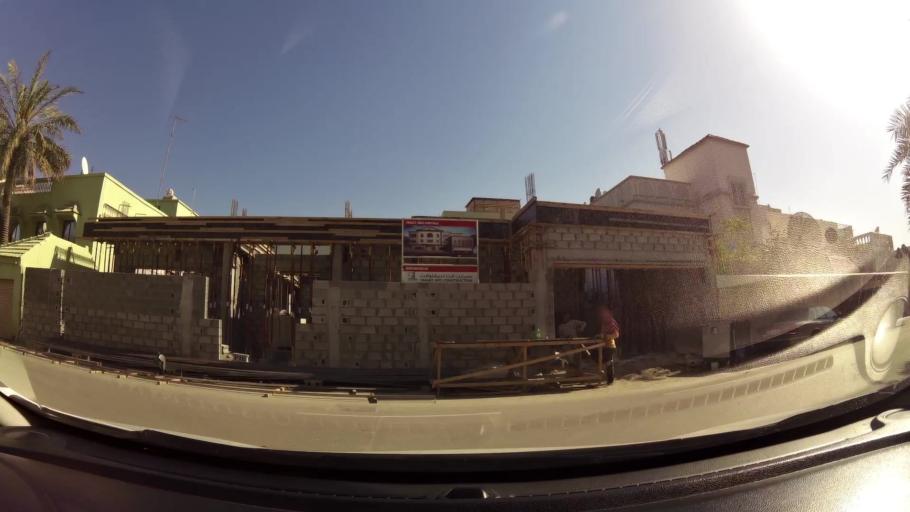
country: BH
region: Manama
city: Manama
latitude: 26.2092
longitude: 50.5684
